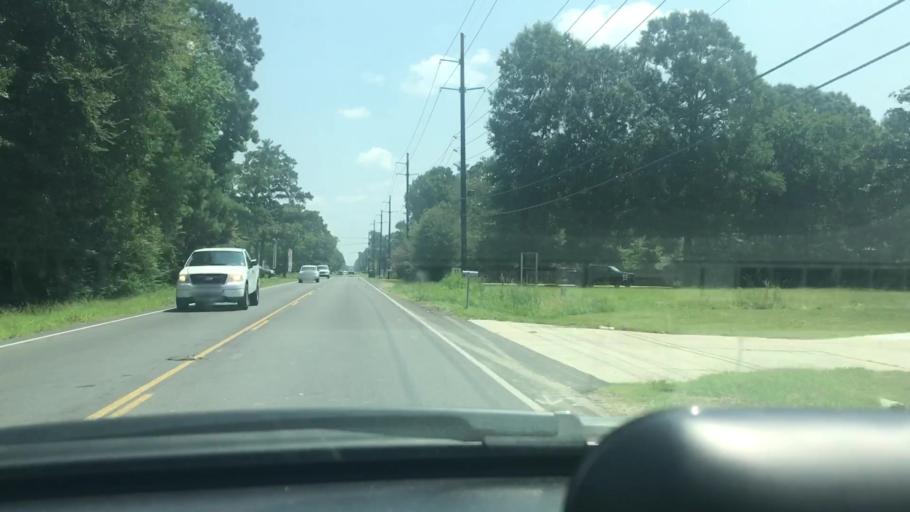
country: US
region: Louisiana
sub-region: Livingston Parish
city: Walker
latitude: 30.4839
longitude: -90.9037
